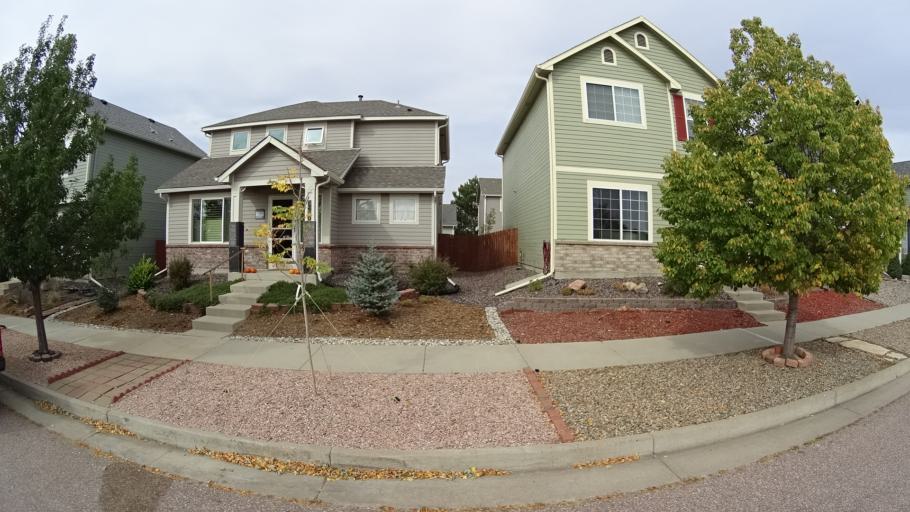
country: US
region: Colorado
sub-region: El Paso County
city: Cimarron Hills
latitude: 38.9207
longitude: -104.7158
